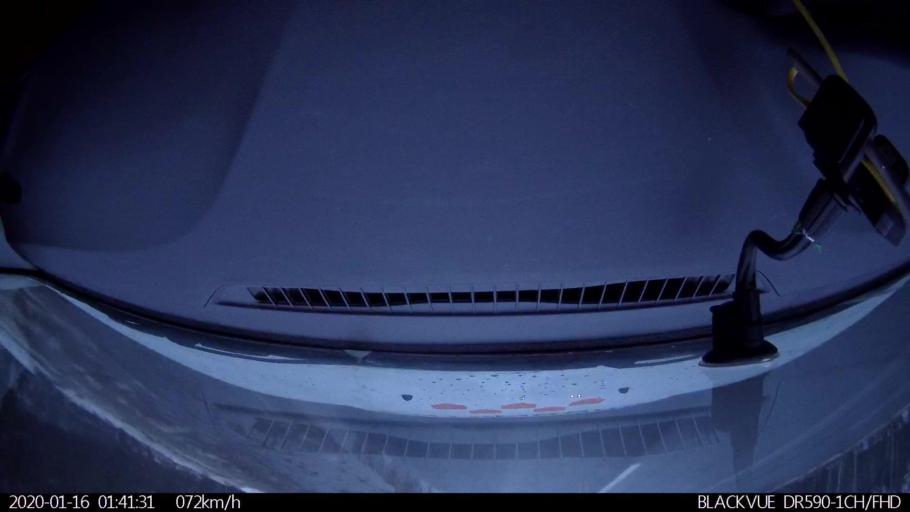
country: RU
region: Nizjnij Novgorod
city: Gorbatovka
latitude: 56.3196
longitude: 43.7657
